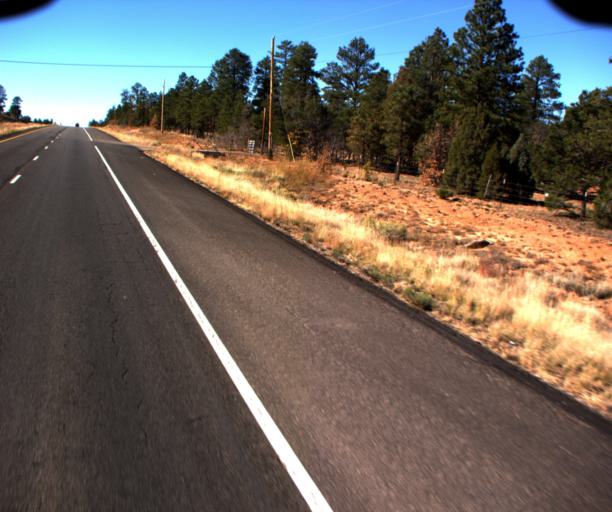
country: US
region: Arizona
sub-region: Apache County
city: Saint Michaels
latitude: 35.6724
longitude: -109.1724
